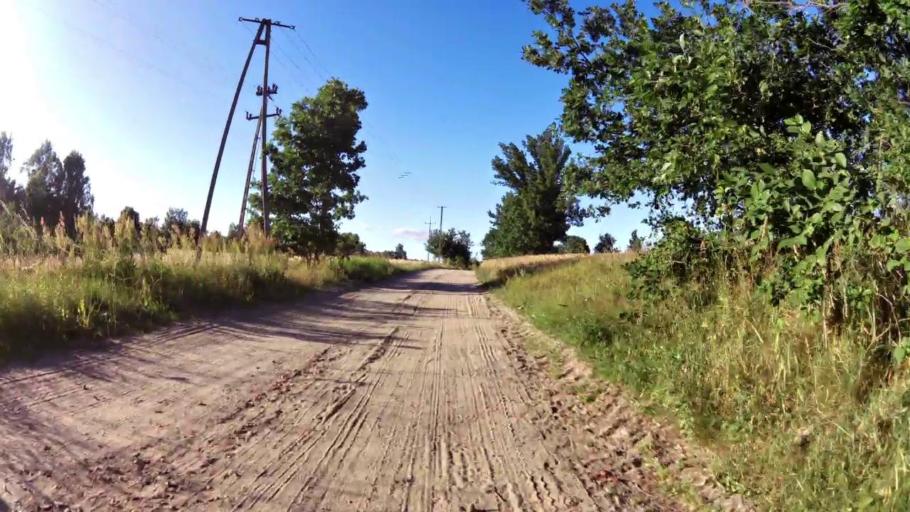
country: PL
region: West Pomeranian Voivodeship
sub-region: Powiat swidwinski
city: Swidwin
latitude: 53.7262
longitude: 15.8379
